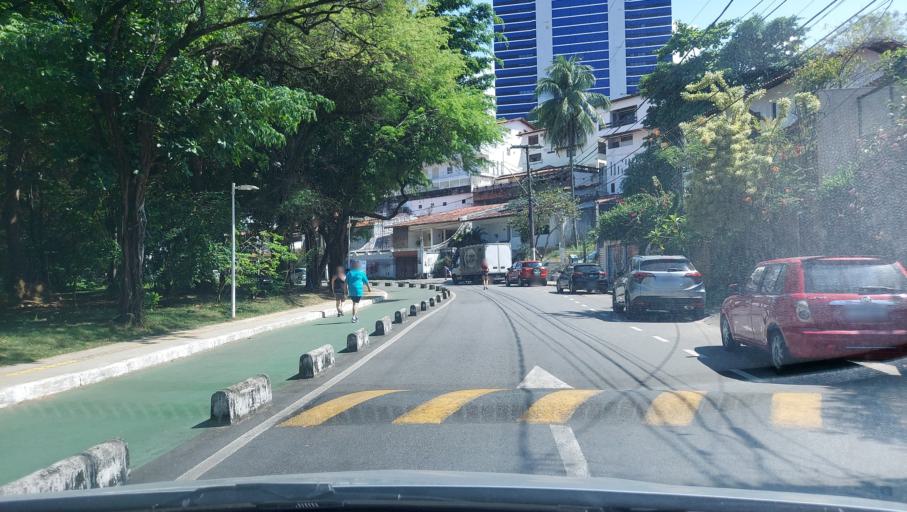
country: BR
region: Bahia
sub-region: Salvador
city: Salvador
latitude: -12.9852
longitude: -38.4555
